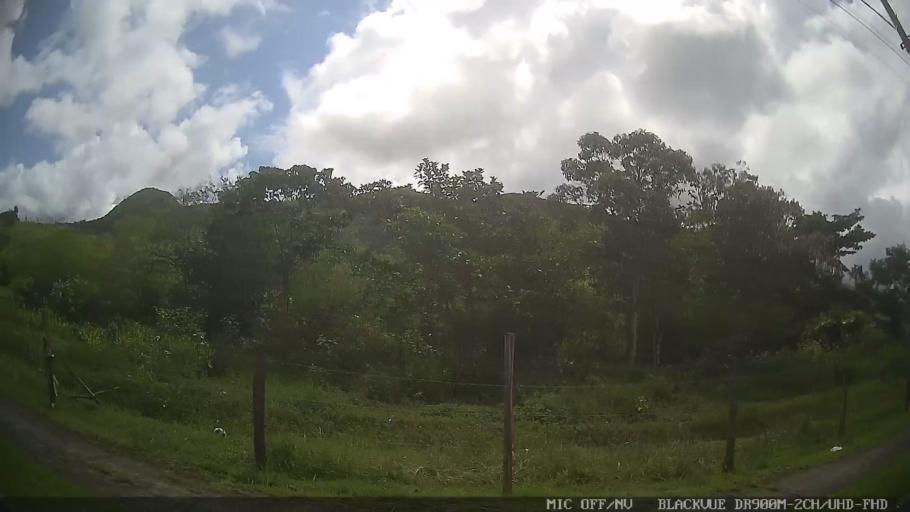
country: BR
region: Sao Paulo
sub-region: Caraguatatuba
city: Caraguatatuba
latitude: -23.6105
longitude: -45.3775
